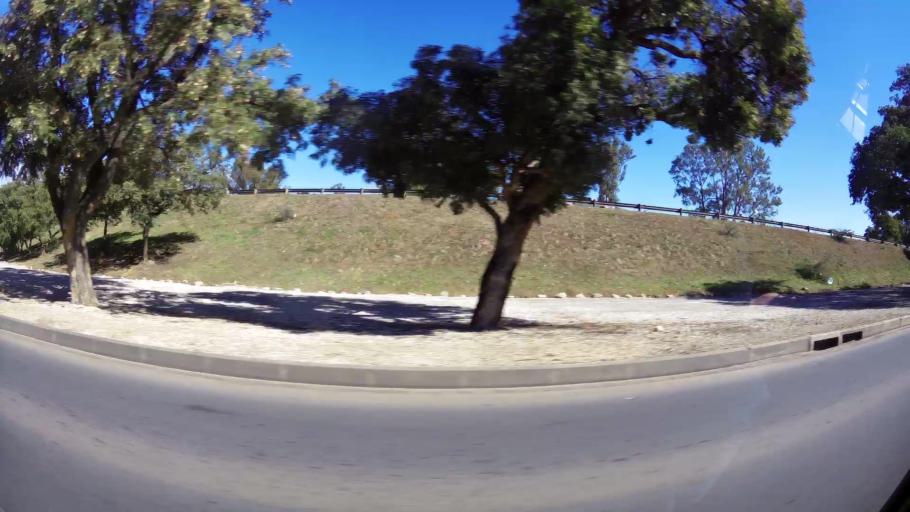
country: ZA
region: Western Cape
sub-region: Cape Winelands District Municipality
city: Ashton
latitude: -33.8101
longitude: 19.8802
